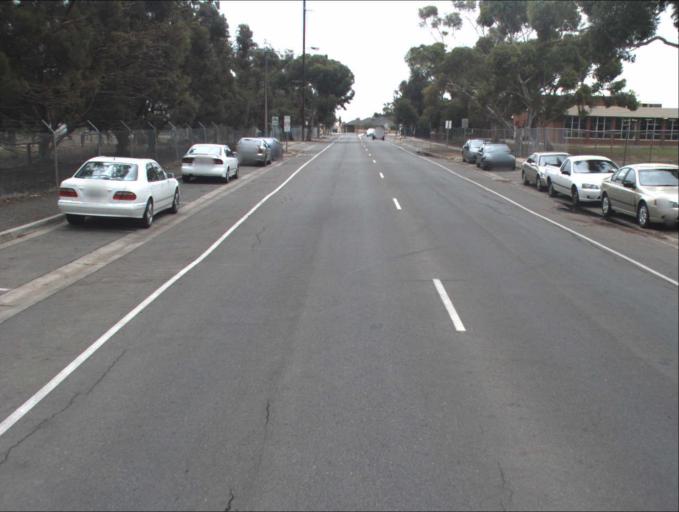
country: AU
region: South Australia
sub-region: Port Adelaide Enfield
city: Gilles Plains
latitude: -34.8481
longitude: 138.6534
